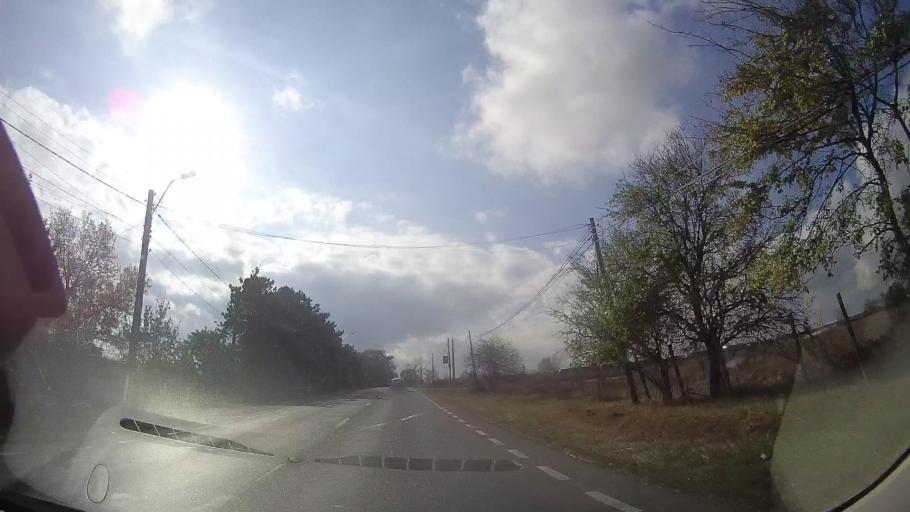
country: RO
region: Constanta
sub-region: Comuna Agigea
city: Agigea
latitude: 44.0863
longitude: 28.6082
